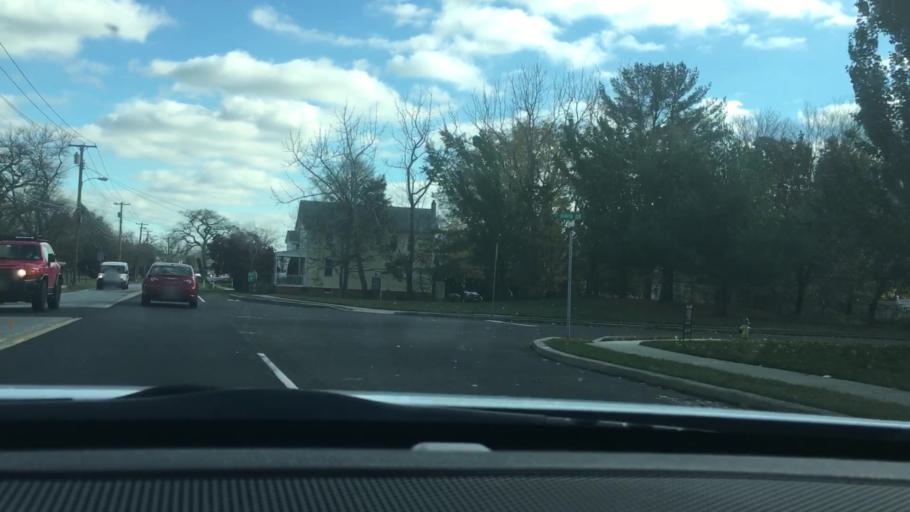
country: US
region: New Jersey
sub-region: Atlantic County
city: Northfield
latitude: 39.3749
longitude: -74.5702
